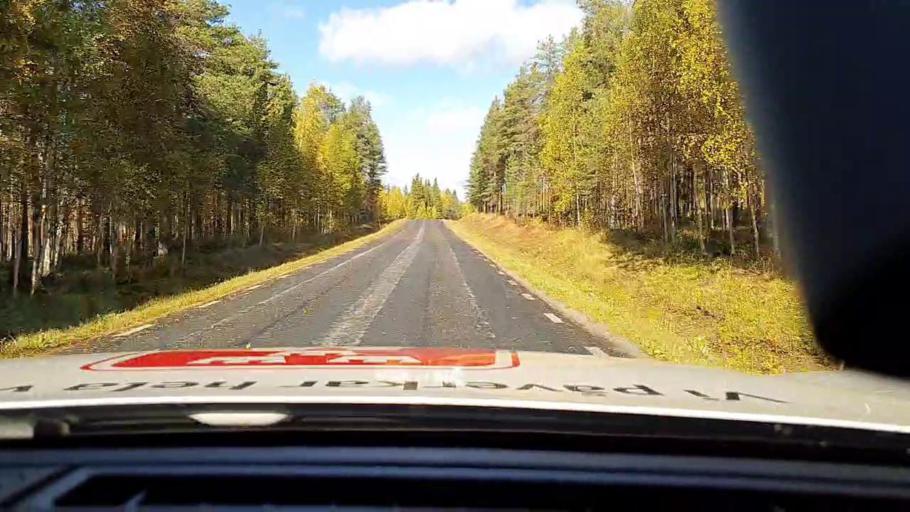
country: SE
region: Vaesterbotten
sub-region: Skelleftea Kommun
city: Langsele
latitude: 65.0164
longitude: 20.0772
